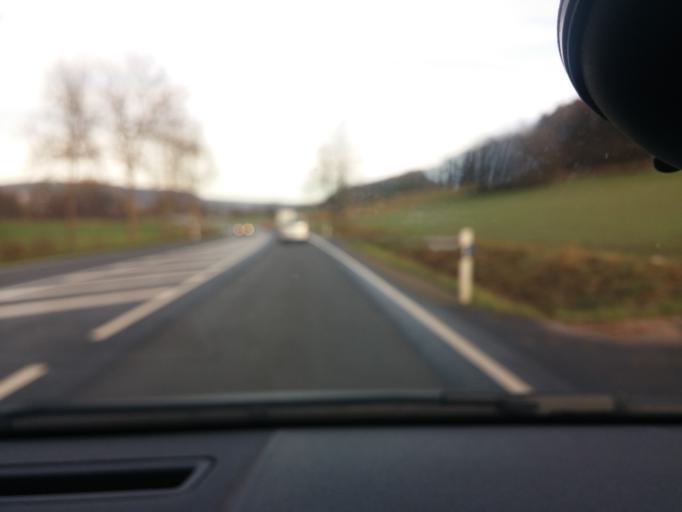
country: DE
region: Hesse
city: Hochst im Odenwald
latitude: 49.7784
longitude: 8.9941
